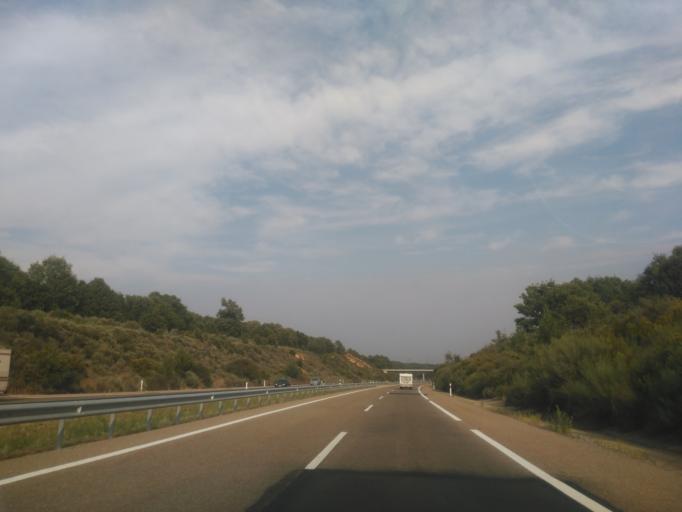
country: ES
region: Castille and Leon
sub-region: Provincia de Zamora
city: Palacios de Sanabria
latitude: 42.0474
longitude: -6.5179
